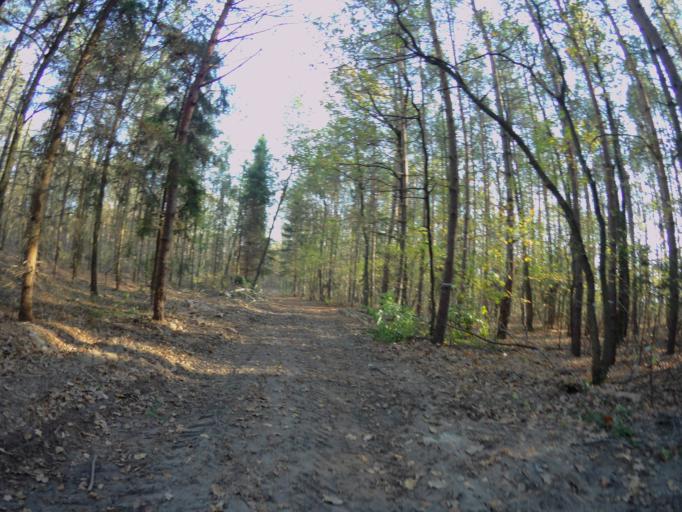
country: PL
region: Subcarpathian Voivodeship
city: Nowa Sarzyna
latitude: 50.3057
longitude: 22.3545
